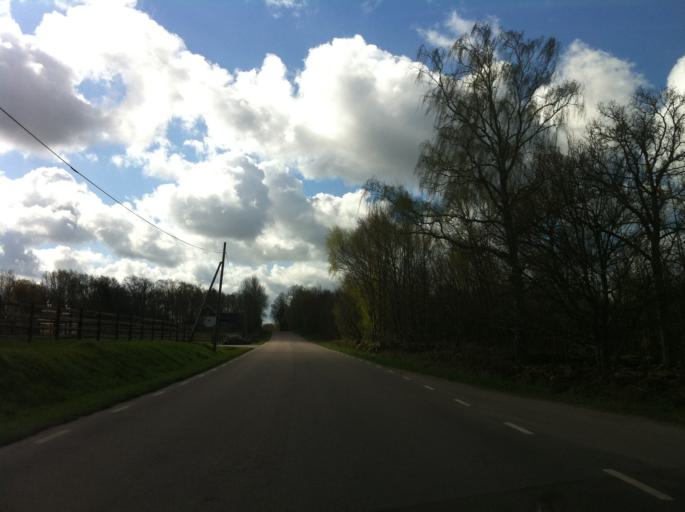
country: SE
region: Skane
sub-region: Horby Kommun
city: Hoerby
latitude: 55.8888
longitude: 13.6157
